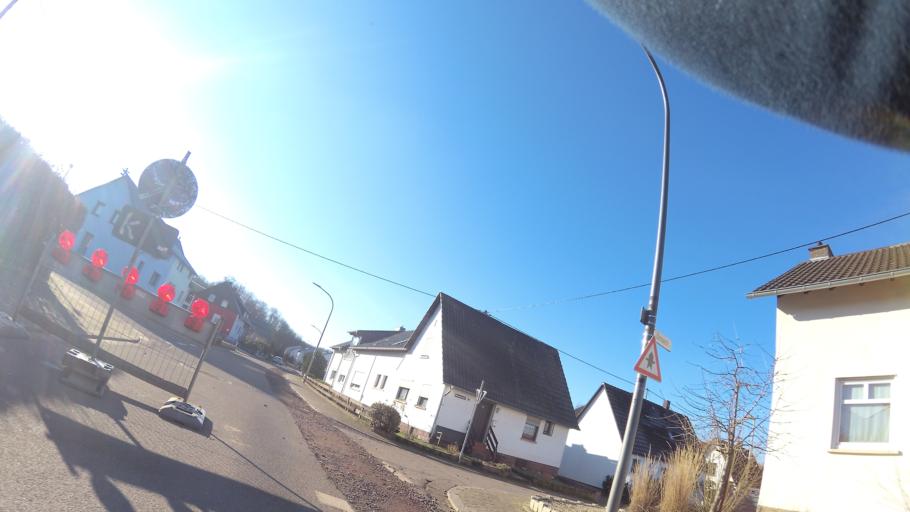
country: DE
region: Saarland
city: Wallerfangen
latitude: 49.3097
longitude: 6.7151
